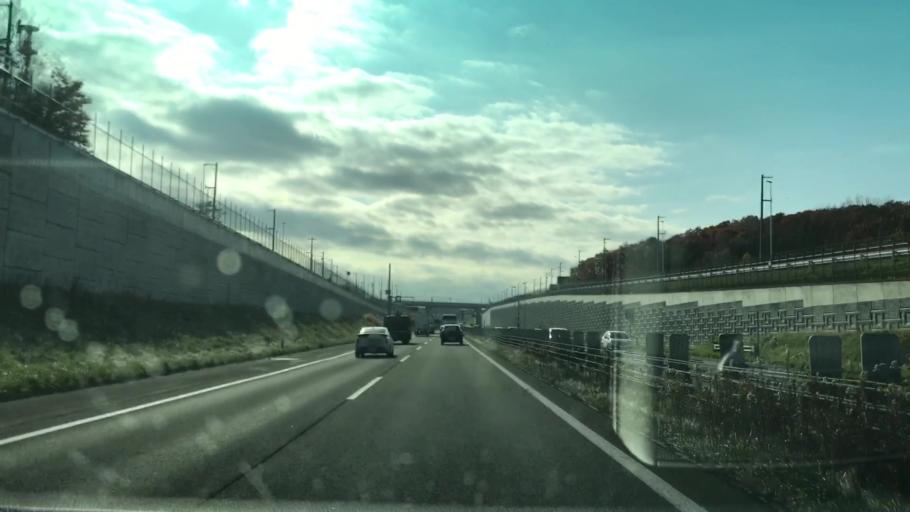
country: JP
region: Hokkaido
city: Kitahiroshima
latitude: 42.9979
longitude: 141.4684
